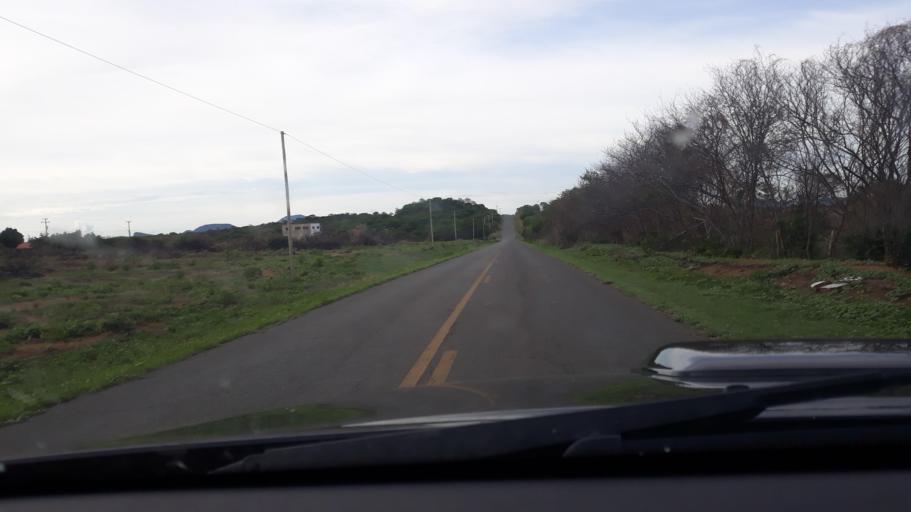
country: BR
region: Bahia
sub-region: Guanambi
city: Guanambi
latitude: -13.9282
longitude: -42.8475
